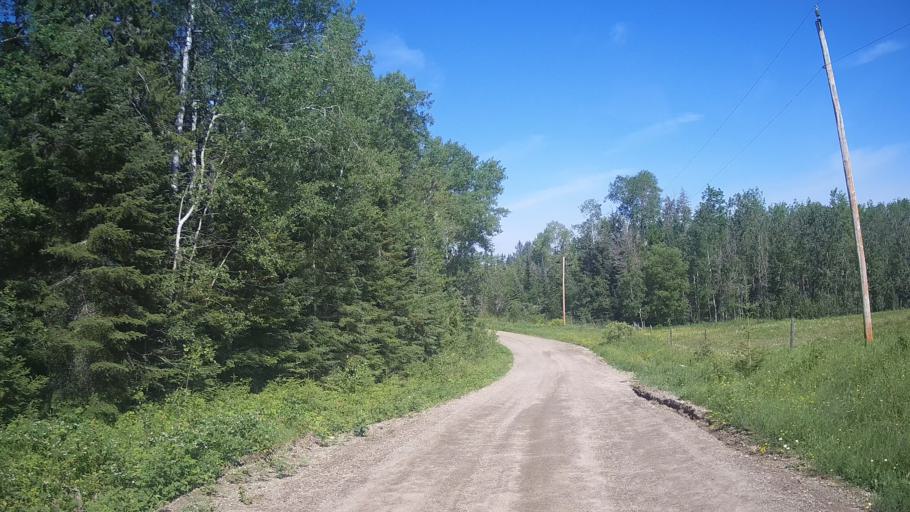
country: CA
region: Ontario
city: Dryden
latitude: 49.8168
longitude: -93.3303
